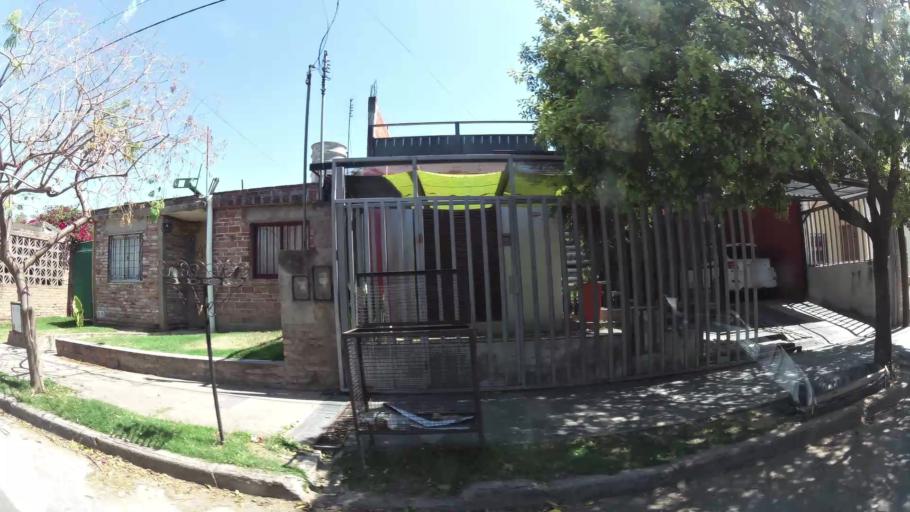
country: AR
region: Cordoba
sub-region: Departamento de Capital
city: Cordoba
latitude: -31.4534
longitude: -64.1631
